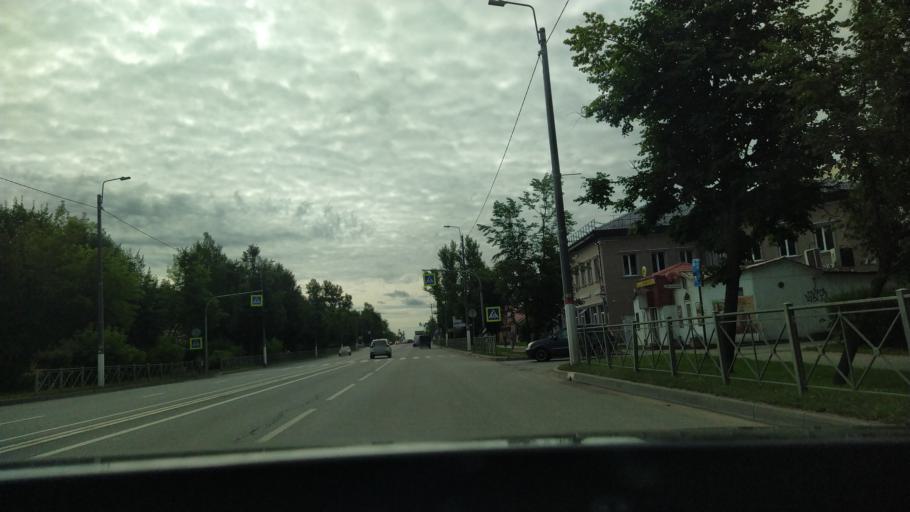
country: RU
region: Leningrad
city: Tosno
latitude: 59.5470
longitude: 30.8660
